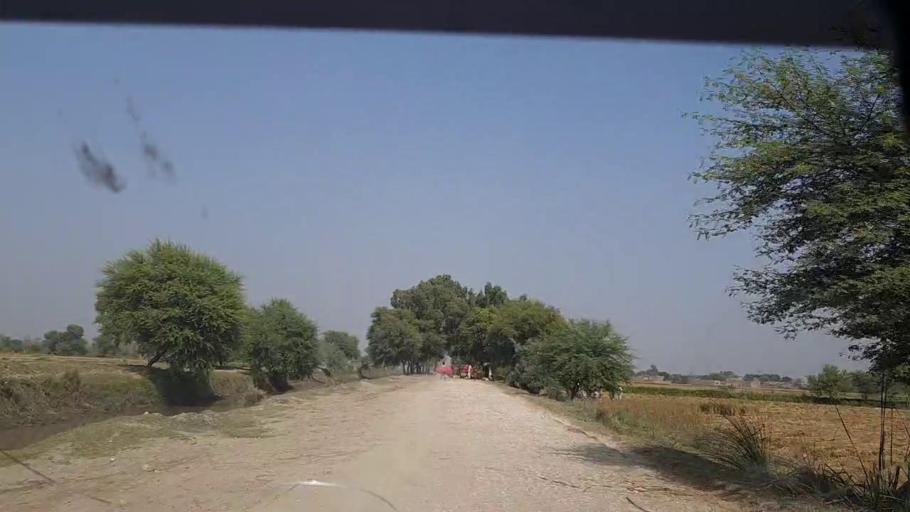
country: PK
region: Sindh
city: Thul
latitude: 28.1089
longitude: 68.6935
